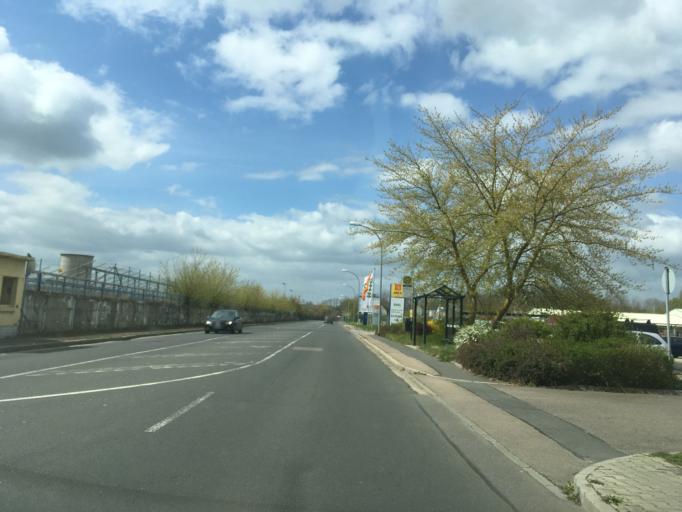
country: DE
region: Saxony
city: Delitzsch
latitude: 51.5179
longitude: 12.3283
